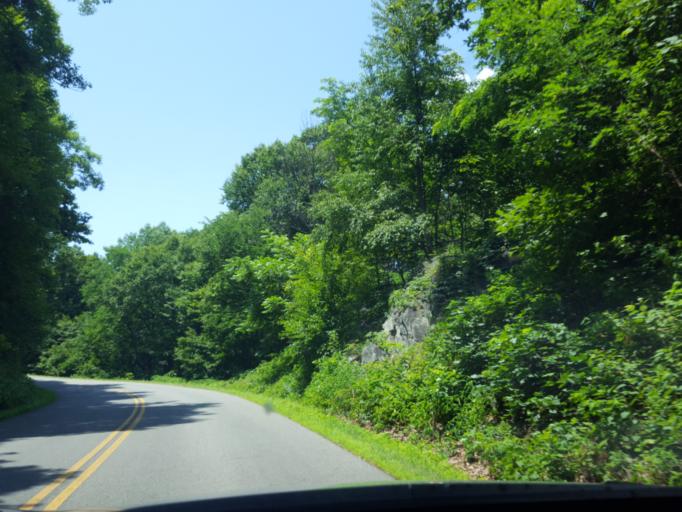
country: US
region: Virginia
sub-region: Nelson County
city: Nellysford
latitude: 37.9418
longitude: -78.9386
